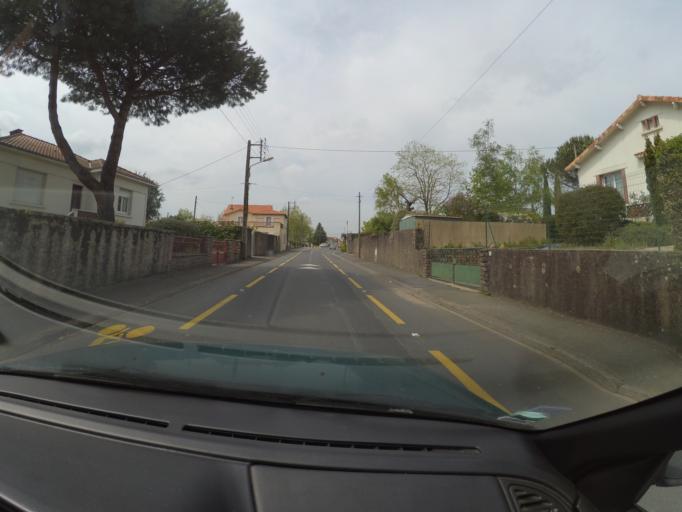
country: FR
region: Pays de la Loire
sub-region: Departement de la Loire-Atlantique
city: Clisson
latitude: 47.0911
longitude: -1.2887
